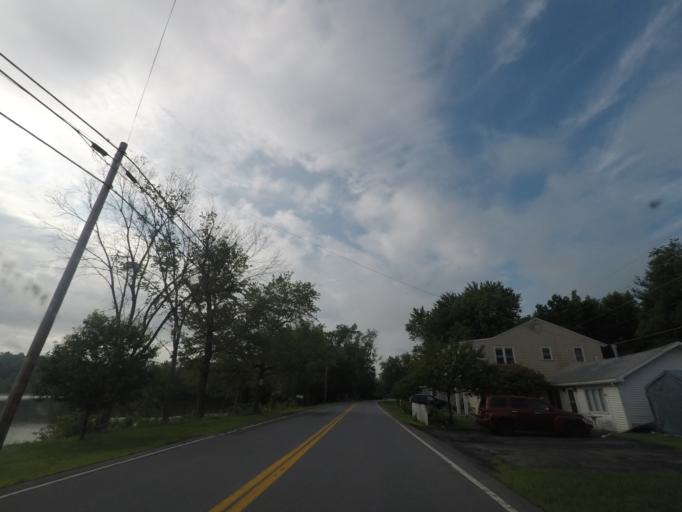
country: US
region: New York
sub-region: Rensselaer County
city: Nassau
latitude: 42.5356
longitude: -73.6086
